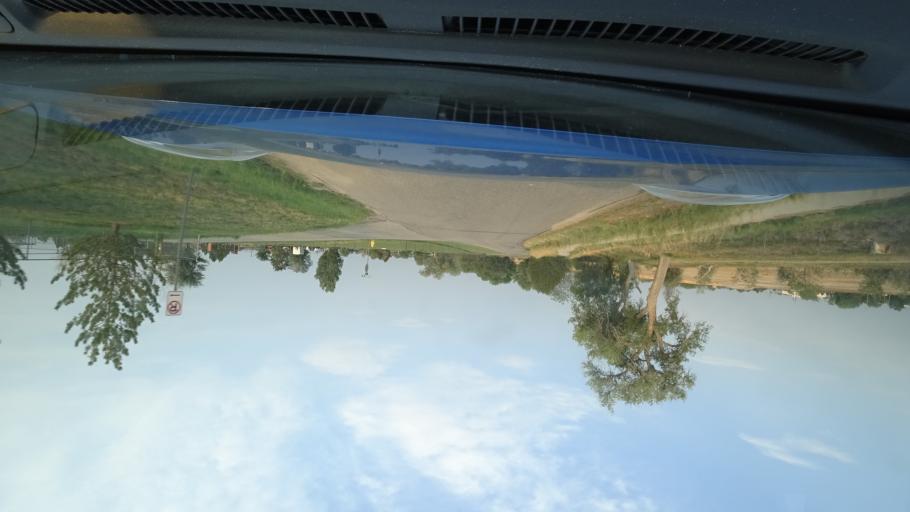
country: US
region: Colorado
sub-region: Adams County
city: Aurora
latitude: 39.7390
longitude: -104.7869
